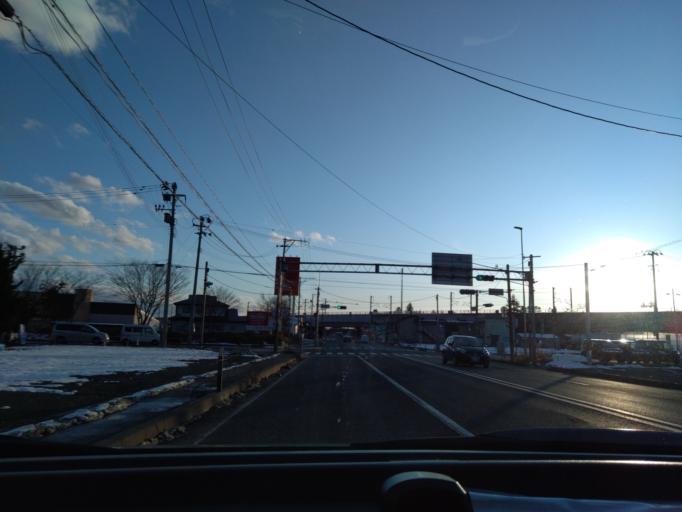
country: JP
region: Iwate
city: Hanamaki
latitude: 39.5380
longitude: 141.1681
